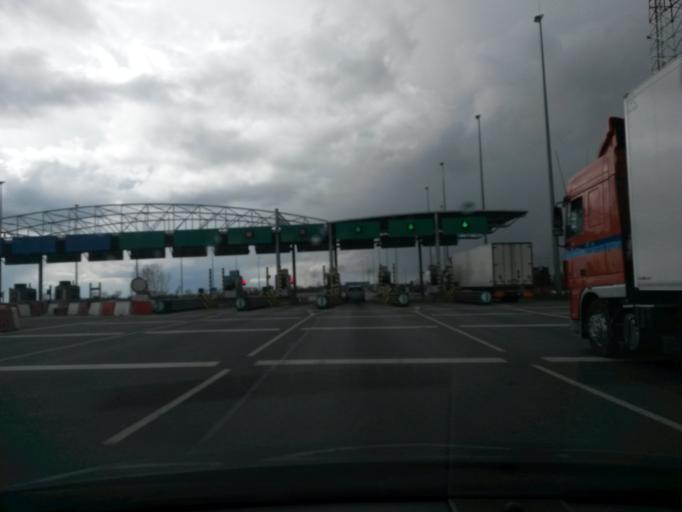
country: PL
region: Greater Poland Voivodeship
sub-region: Powiat poznanski
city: Kleszczewo
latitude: 52.3108
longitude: 17.1521
